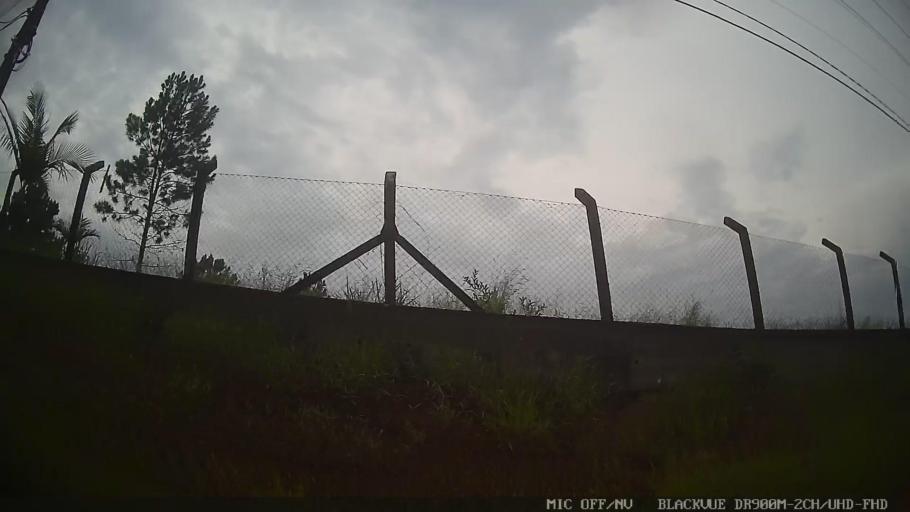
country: BR
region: Sao Paulo
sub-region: Suzano
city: Suzano
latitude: -23.6402
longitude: -46.2906
